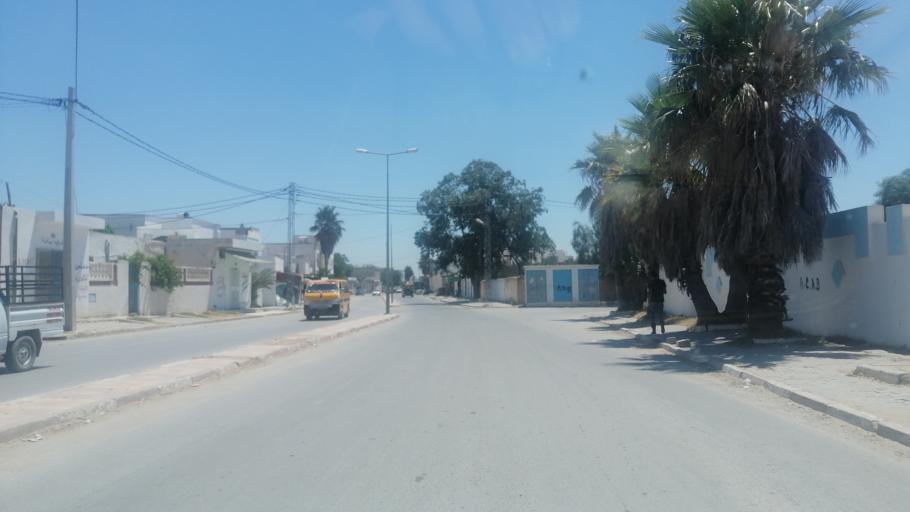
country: TN
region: Al Qayrawan
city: Sbikha
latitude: 36.1203
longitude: 10.0902
